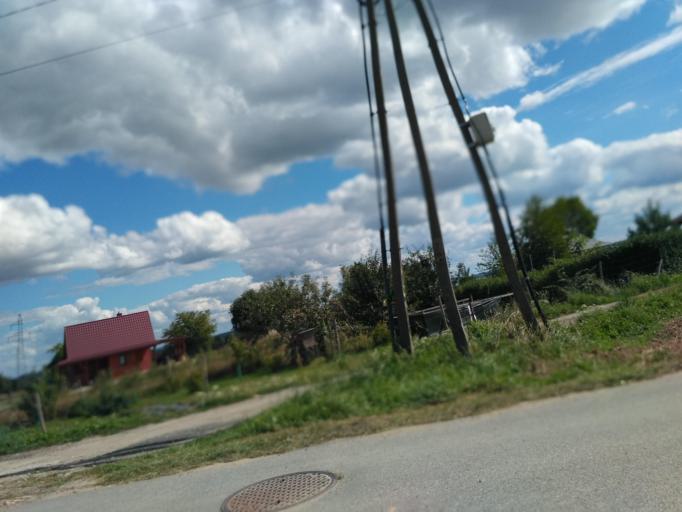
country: PL
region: Subcarpathian Voivodeship
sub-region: Powiat jasielski
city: Jaslo
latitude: 49.7609
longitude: 21.5073
